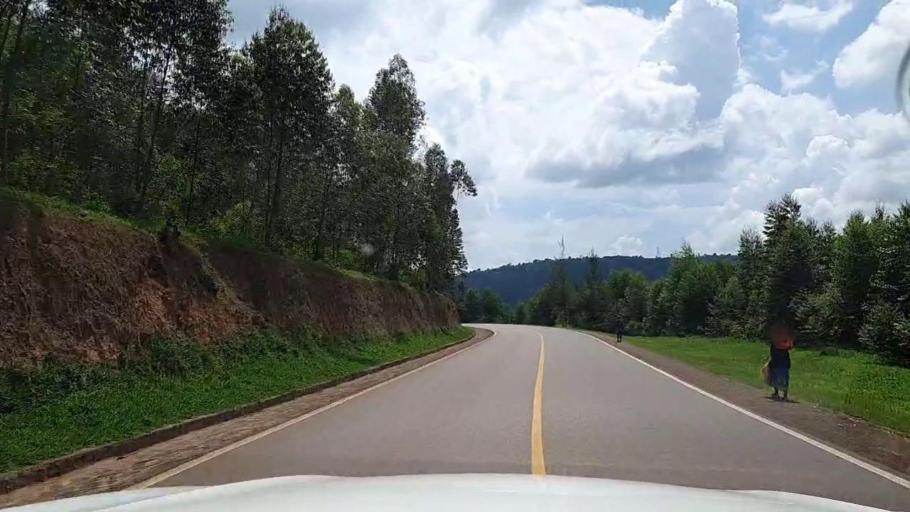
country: RW
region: Kigali
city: Kigali
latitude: -1.8130
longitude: 30.1043
